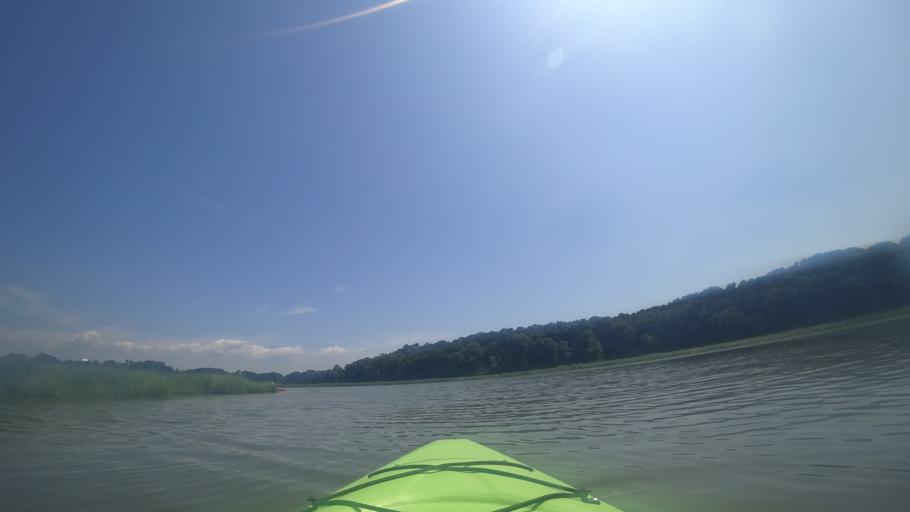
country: US
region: Virginia
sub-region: Isle of Wight County
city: Smithfield
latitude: 36.9710
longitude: -76.6169
